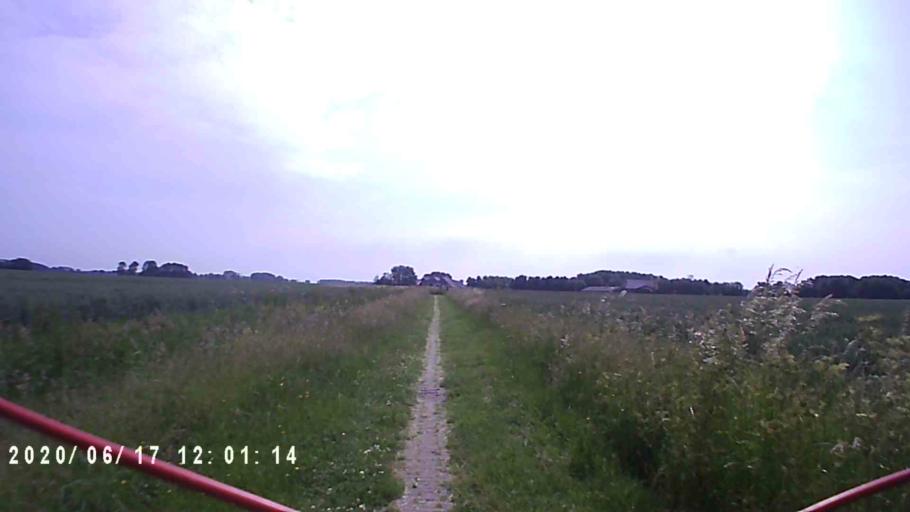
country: NL
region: Groningen
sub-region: Gemeente De Marne
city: Ulrum
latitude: 53.3413
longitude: 6.3346
